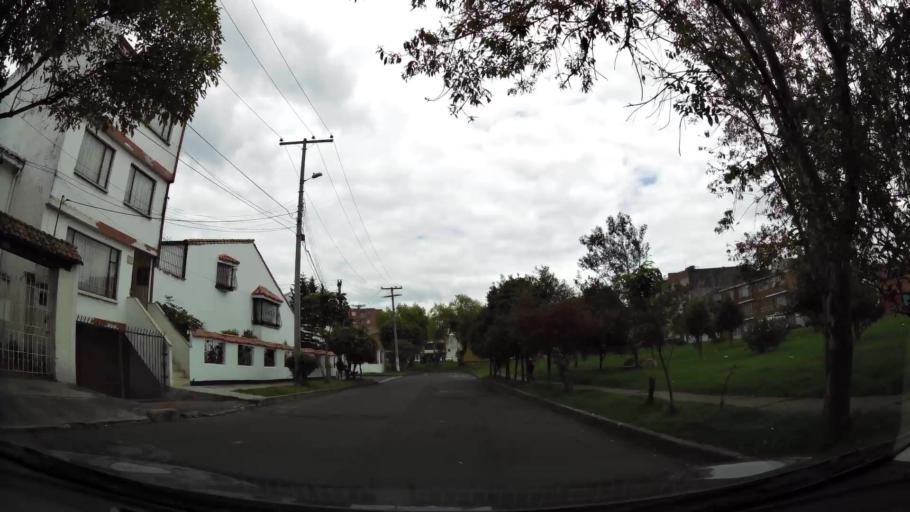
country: CO
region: Bogota D.C.
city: Barrio San Luis
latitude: 4.7147
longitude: -74.0651
